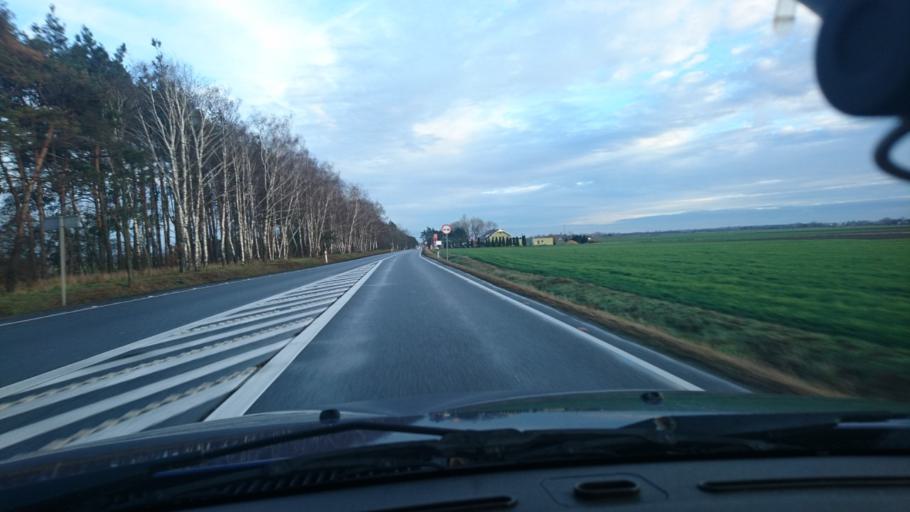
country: PL
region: Greater Poland Voivodeship
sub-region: Powiat kepinski
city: Leka Opatowska
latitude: 51.2242
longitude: 18.1098
